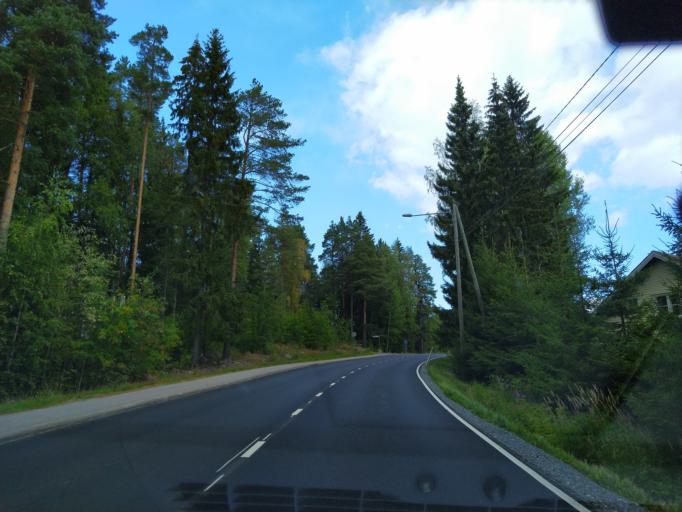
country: FI
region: Pirkanmaa
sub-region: Tampere
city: Kuru
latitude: 61.8900
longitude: 23.7400
